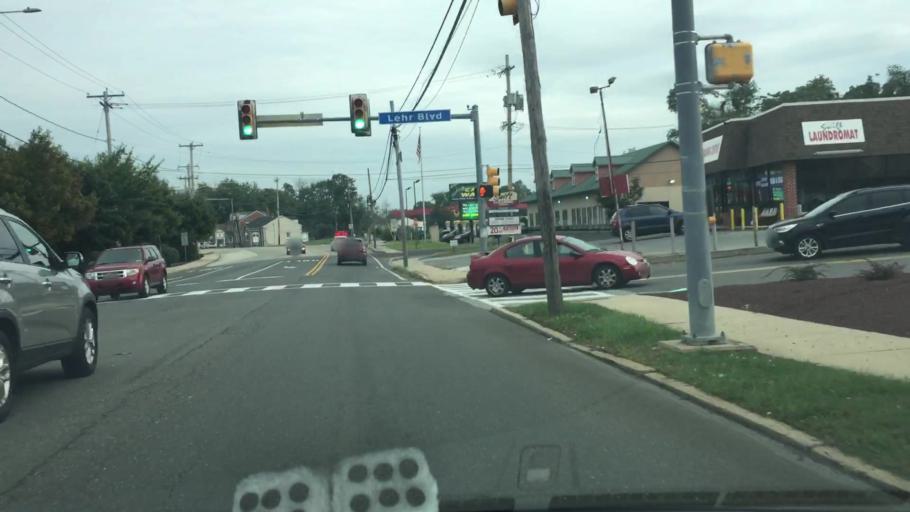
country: US
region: Pennsylvania
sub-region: Delaware County
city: Village Green-Green Ridge
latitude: 39.8673
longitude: -75.4258
